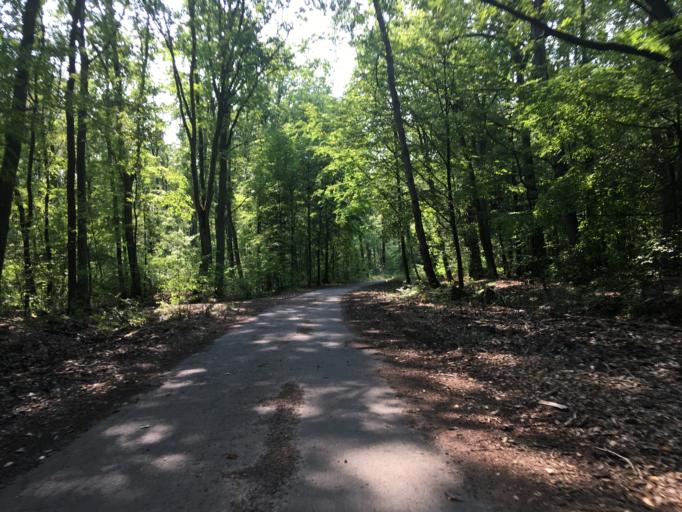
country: DE
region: Berlin
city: Konradshohe
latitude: 52.5944
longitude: 13.1946
